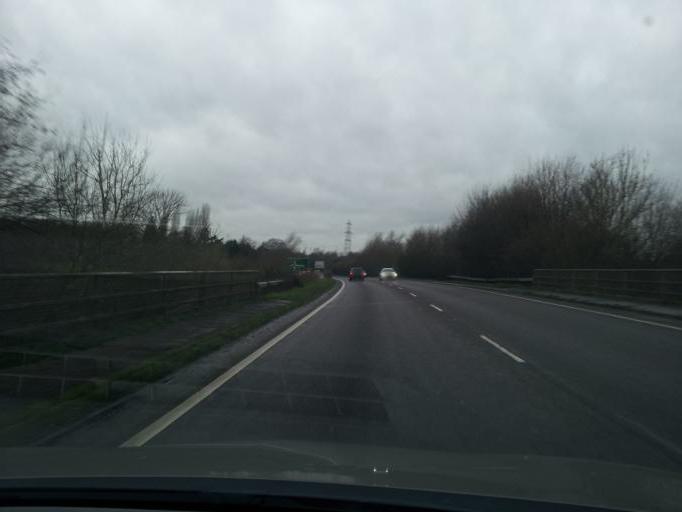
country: GB
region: England
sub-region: Norfolk
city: Diss
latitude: 52.3624
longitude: 1.1535
